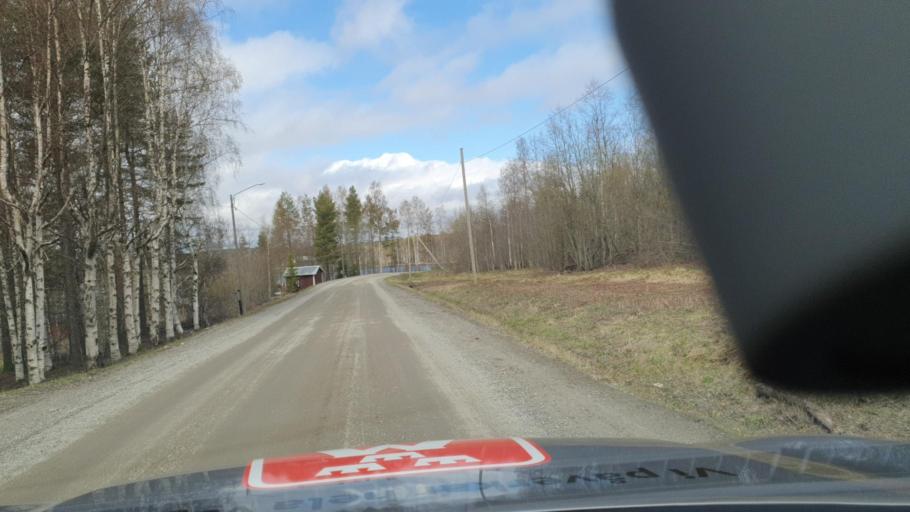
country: SE
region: Vaesterbotten
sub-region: Bjurholms Kommun
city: Bjurholm
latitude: 63.6898
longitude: 18.9576
